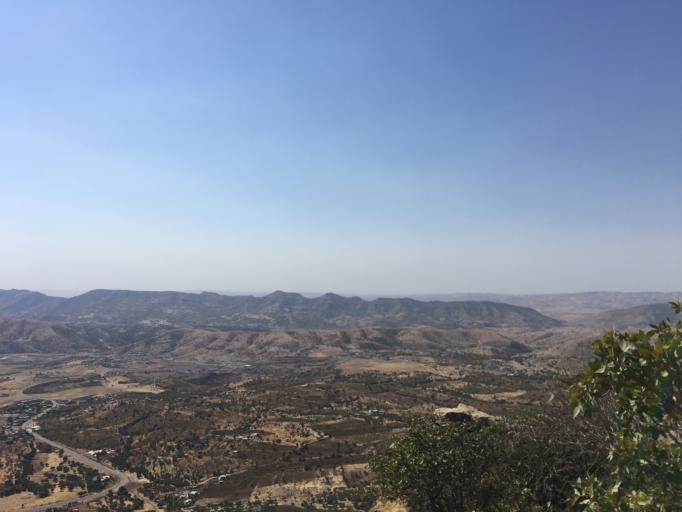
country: IQ
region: Arbil
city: Nahiyat Hiran
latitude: 36.3087
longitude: 44.4162
